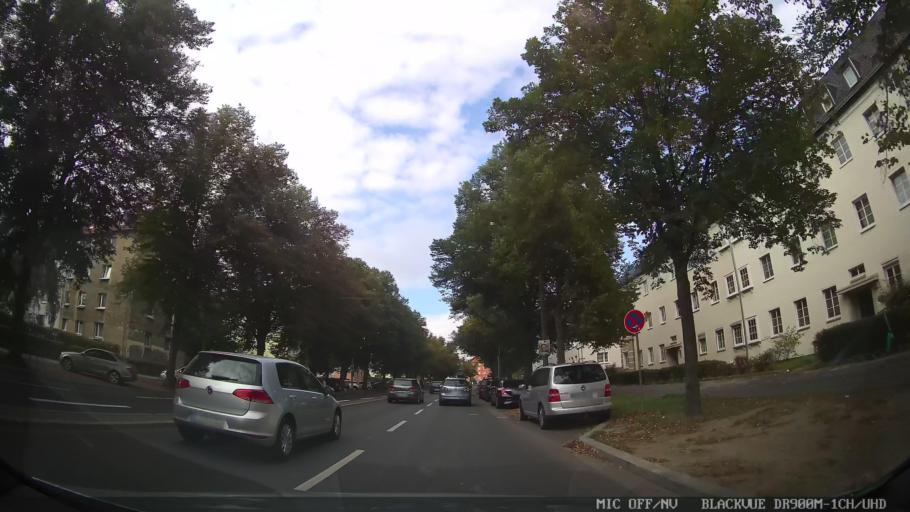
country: DE
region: Lower Saxony
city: Braunschweig
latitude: 52.2554
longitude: 10.5062
